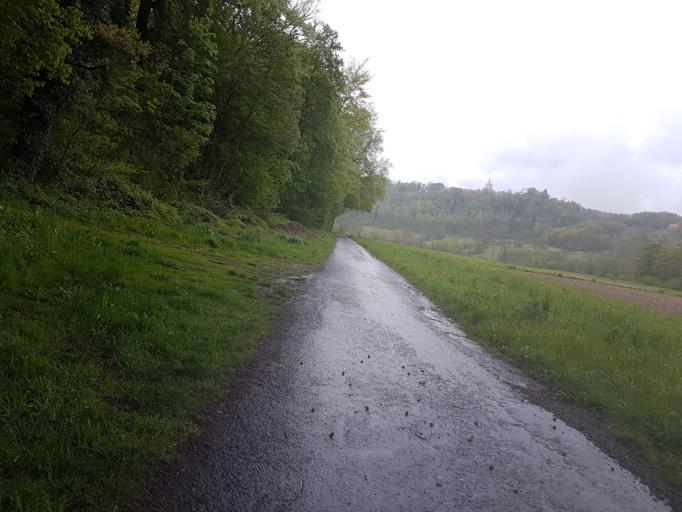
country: CH
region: Vaud
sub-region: Gros-de-Vaud District
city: Penthalaz
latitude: 46.6181
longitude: 6.5223
